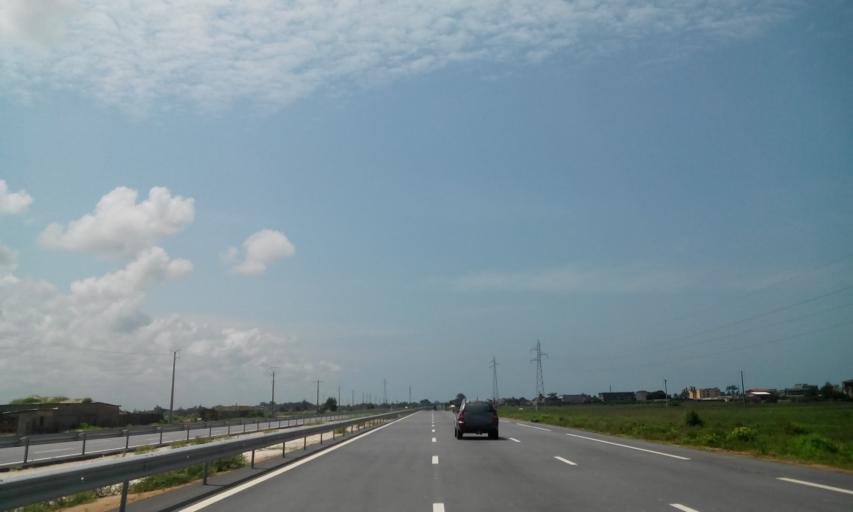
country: CI
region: Sud-Comoe
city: Grand-Bassam
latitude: 5.2277
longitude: -3.7438
